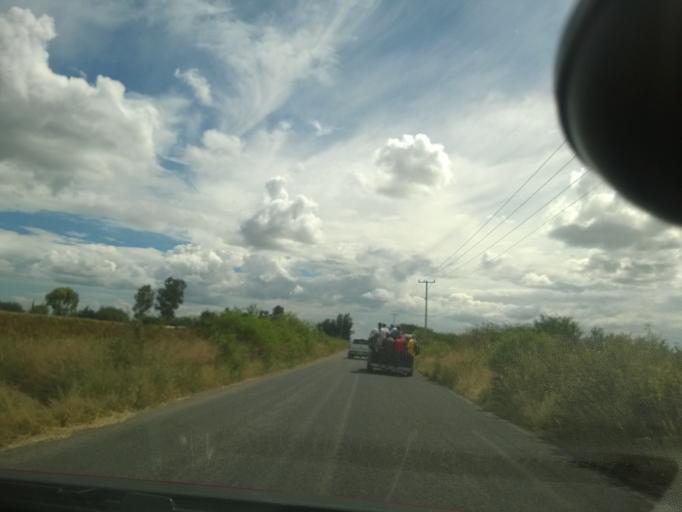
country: MX
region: Guanajuato
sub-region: Leon
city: El CERESO
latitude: 20.9766
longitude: -101.6529
